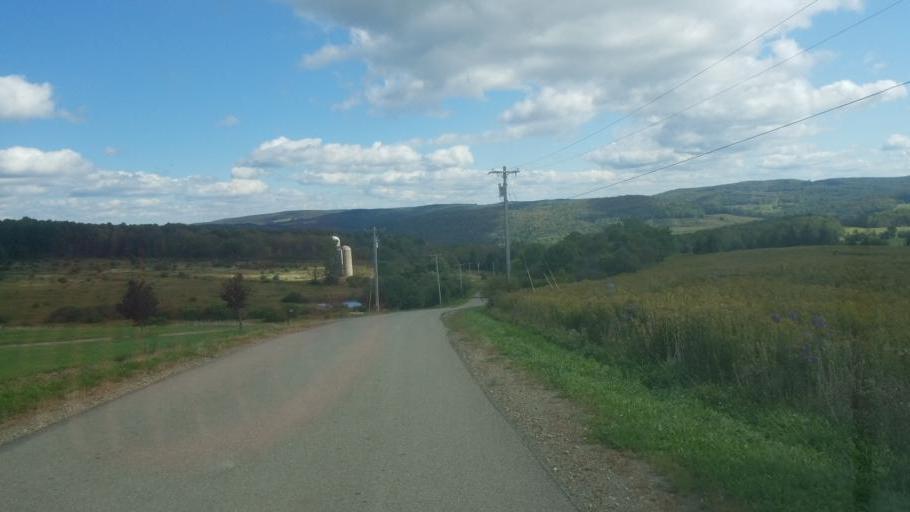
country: US
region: New York
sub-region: Allegany County
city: Cuba
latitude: 42.2014
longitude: -78.2992
